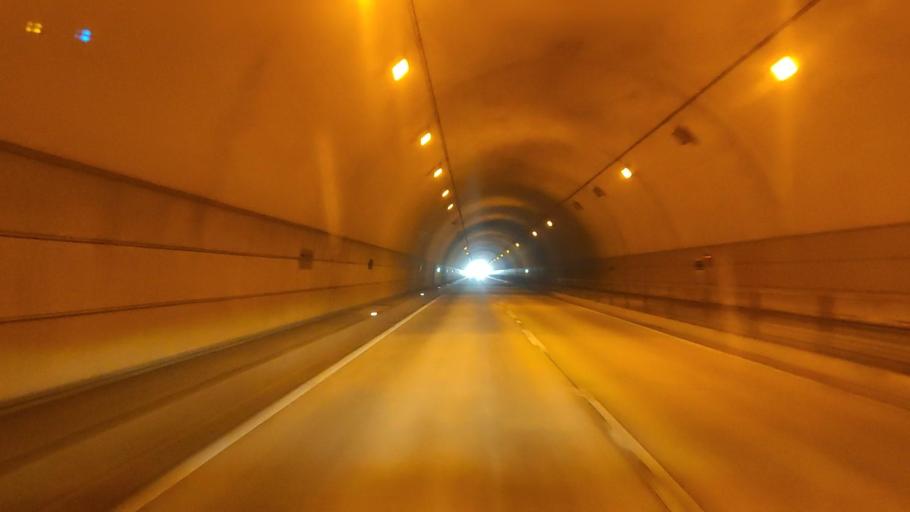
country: JP
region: Miyazaki
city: Nobeoka
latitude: 32.6864
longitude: 131.7932
